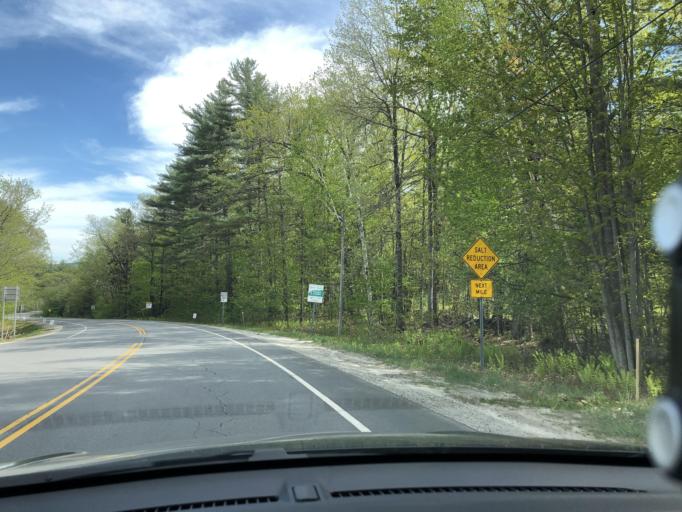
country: US
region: New Hampshire
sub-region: Merrimack County
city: New London
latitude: 43.4216
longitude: -72.0395
